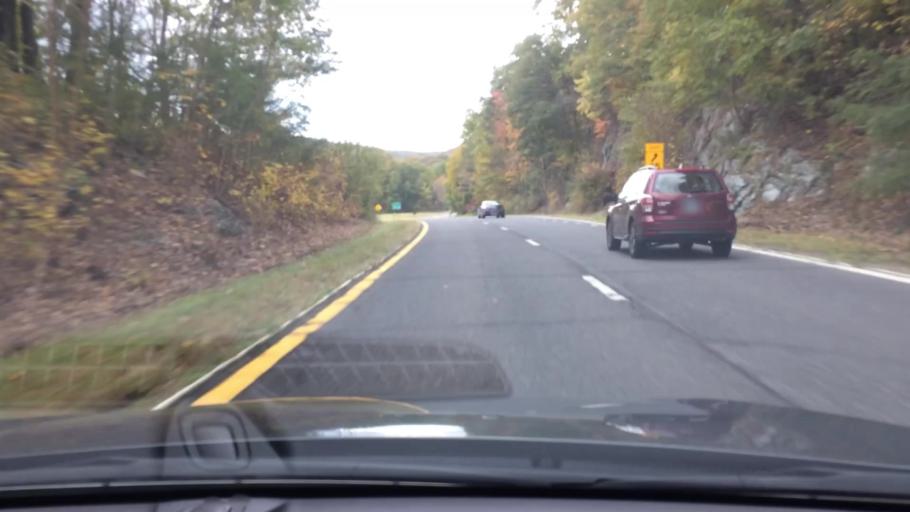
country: US
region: New York
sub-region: Dutchess County
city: Pleasant Valley
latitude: 41.7797
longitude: -73.7695
